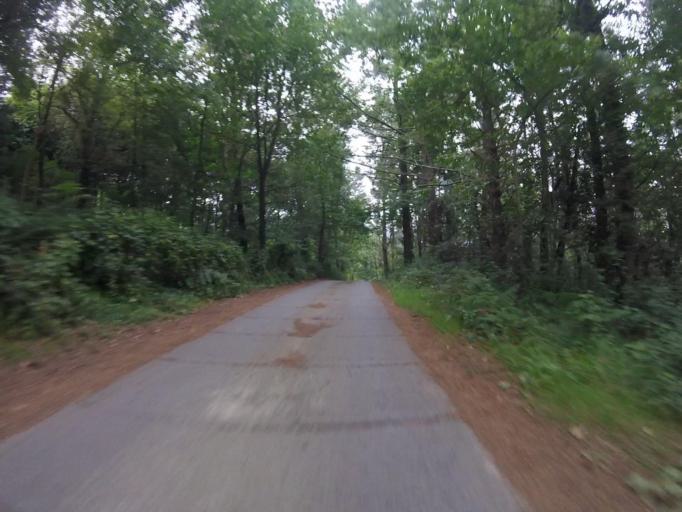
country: ES
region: Basque Country
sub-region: Provincia de Guipuzcoa
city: Lezo
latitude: 43.3119
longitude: -1.8679
